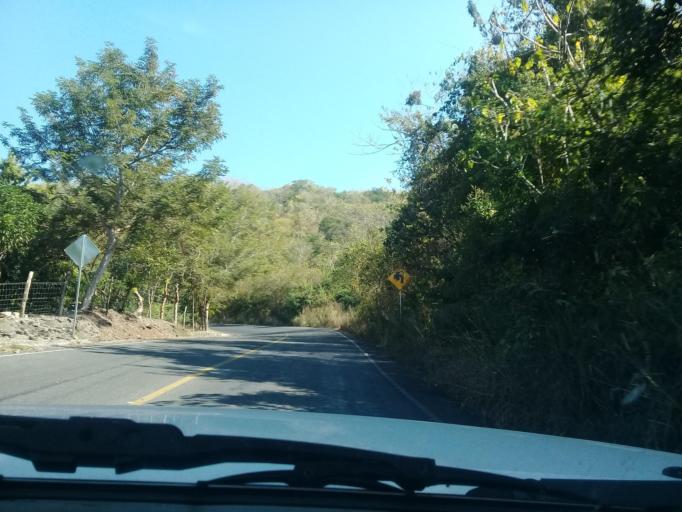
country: MX
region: Veracruz
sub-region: Emiliano Zapata
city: Plan del Rio
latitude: 19.4145
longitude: -96.6139
